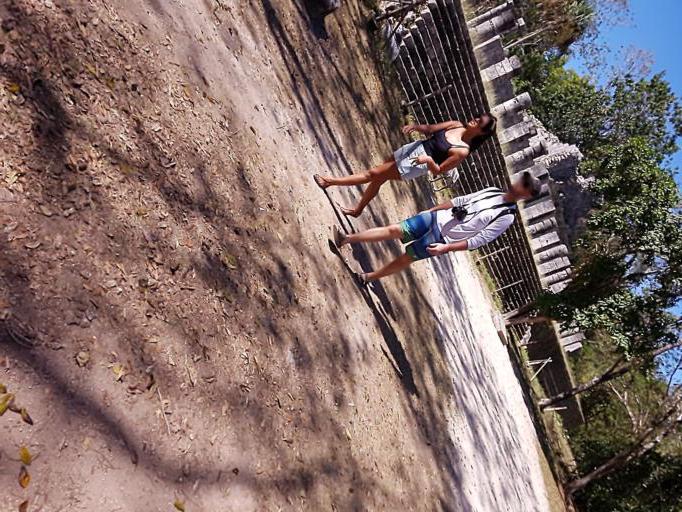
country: MX
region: Yucatan
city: Chichen-Itza
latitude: 20.6812
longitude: -88.5668
